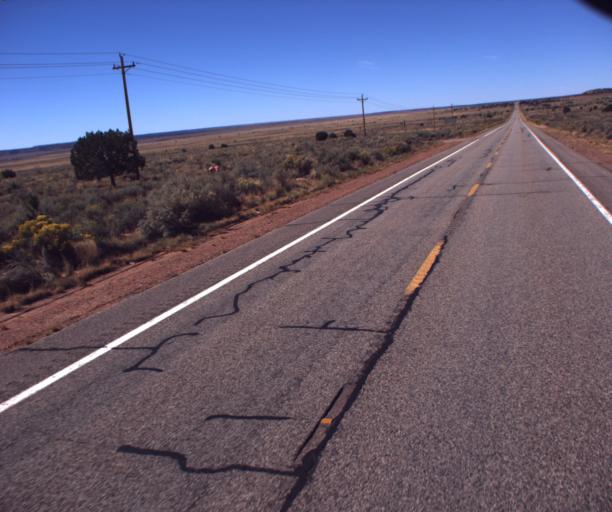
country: US
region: Arizona
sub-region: Coconino County
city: Fredonia
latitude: 36.8577
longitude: -112.7432
